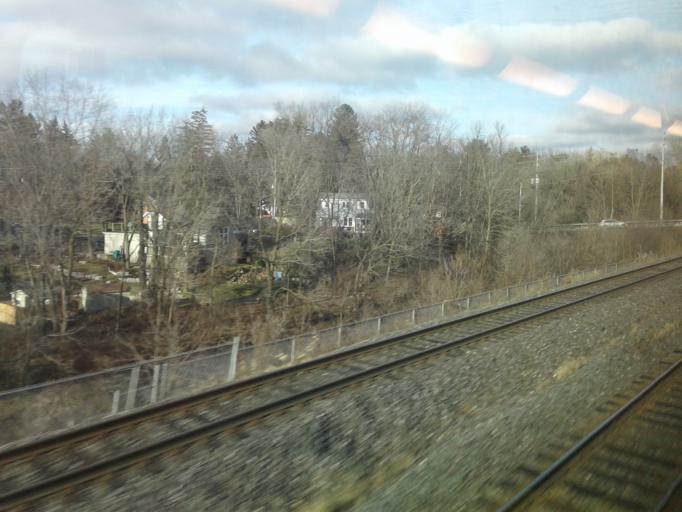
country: CA
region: Ontario
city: Mississauga
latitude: 43.5527
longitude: -79.5909
